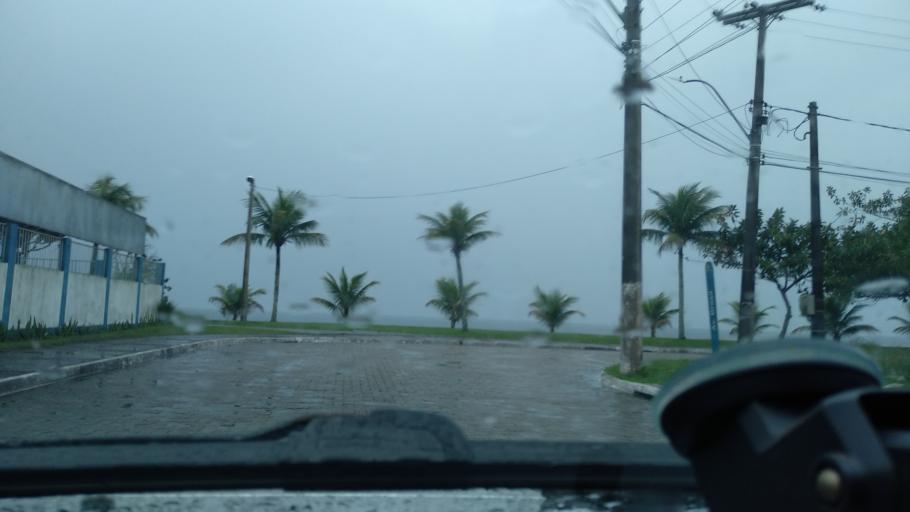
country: BR
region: Rio de Janeiro
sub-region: Angra Dos Reis
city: Angra dos Reis
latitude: -23.0277
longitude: -44.5338
